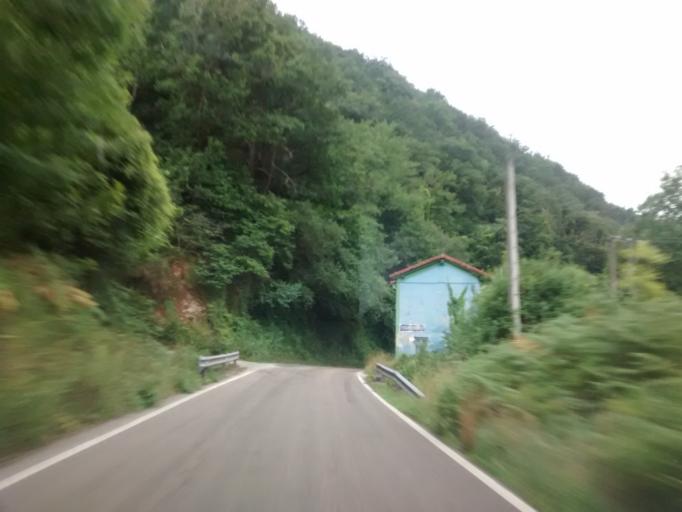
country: ES
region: Cantabria
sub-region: Provincia de Cantabria
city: San Pedro del Romeral
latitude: 43.1691
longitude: -3.8771
